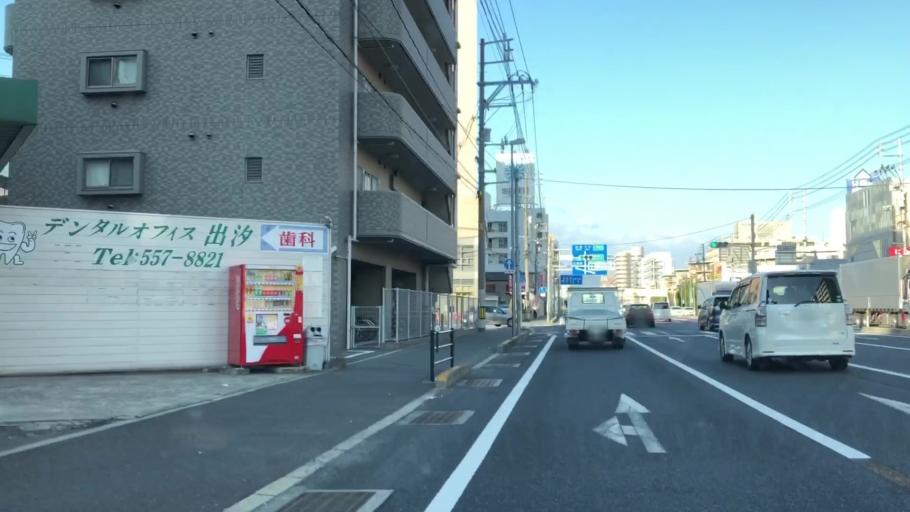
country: JP
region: Hiroshima
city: Hiroshima-shi
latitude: 34.3780
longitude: 132.4758
